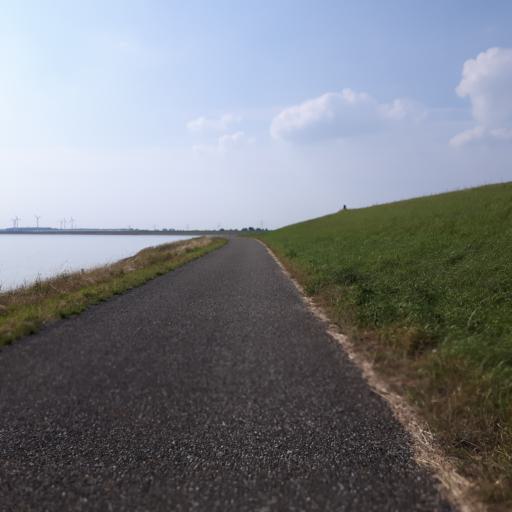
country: NL
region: Zeeland
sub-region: Gemeente Reimerswaal
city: Yerseke
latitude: 51.4602
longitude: 3.9804
